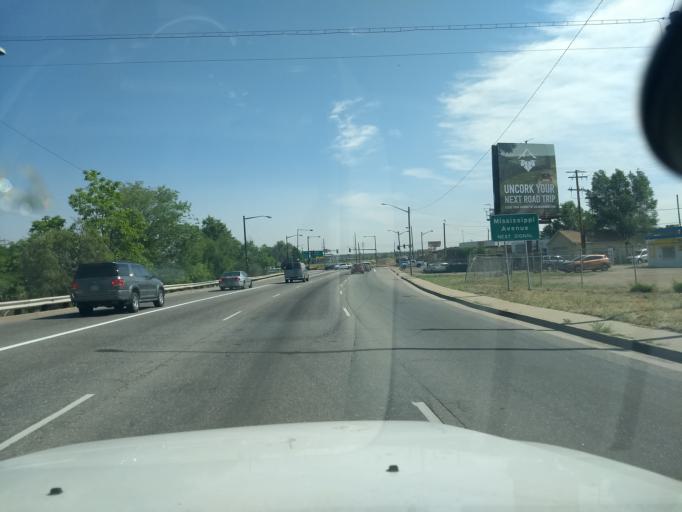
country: US
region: Colorado
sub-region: Denver County
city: Denver
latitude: 39.6953
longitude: -104.9923
